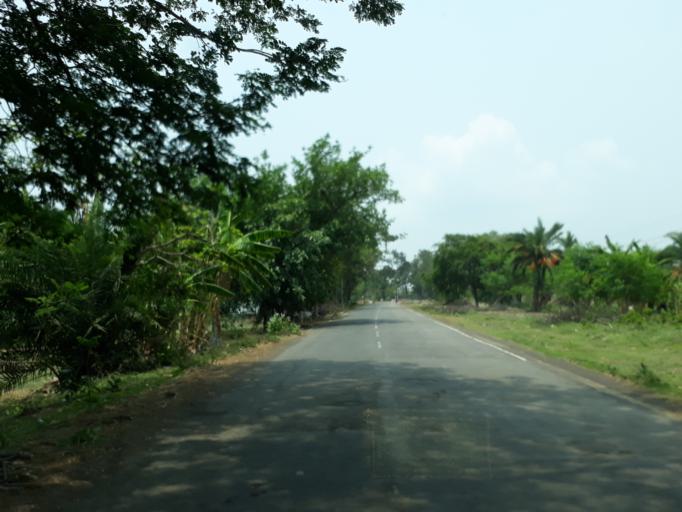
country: IN
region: West Bengal
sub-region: Purba Medinipur
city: Haldia
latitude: 22.0441
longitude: 88.0727
